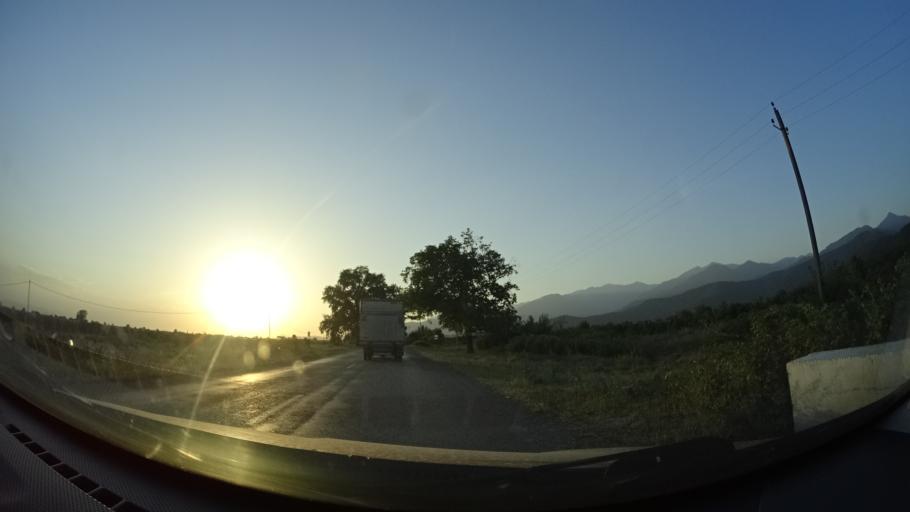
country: GE
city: Bagdadi
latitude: 41.8619
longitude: 46.0210
